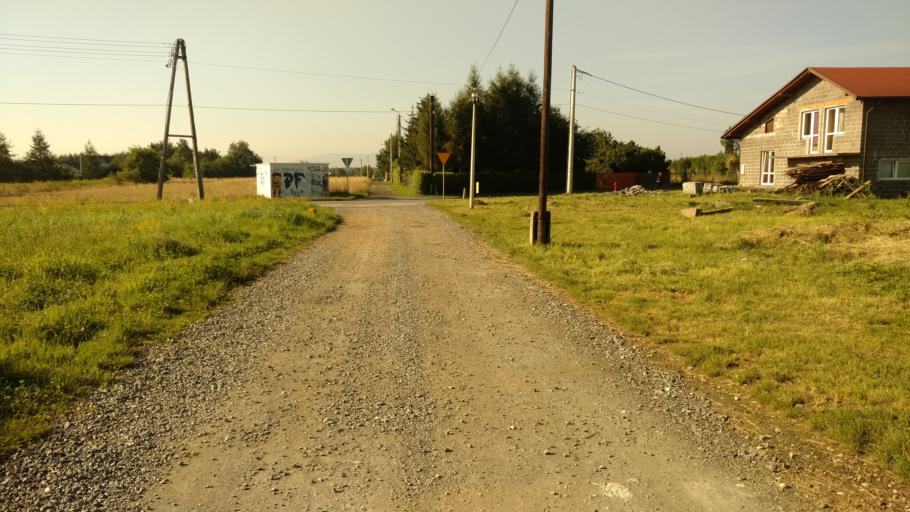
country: PL
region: Silesian Voivodeship
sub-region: Powiat pszczynski
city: Pszczyna
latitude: 49.9895
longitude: 18.9675
